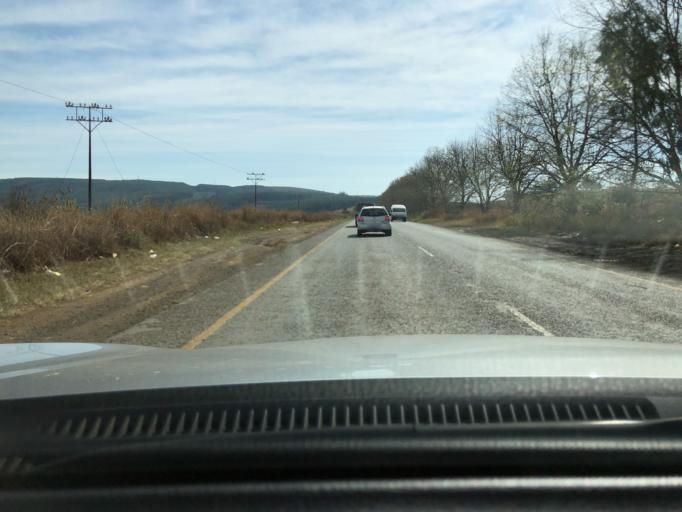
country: ZA
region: KwaZulu-Natal
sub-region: Sisonke District Municipality
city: Ixopo
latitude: -30.1237
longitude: 30.0823
